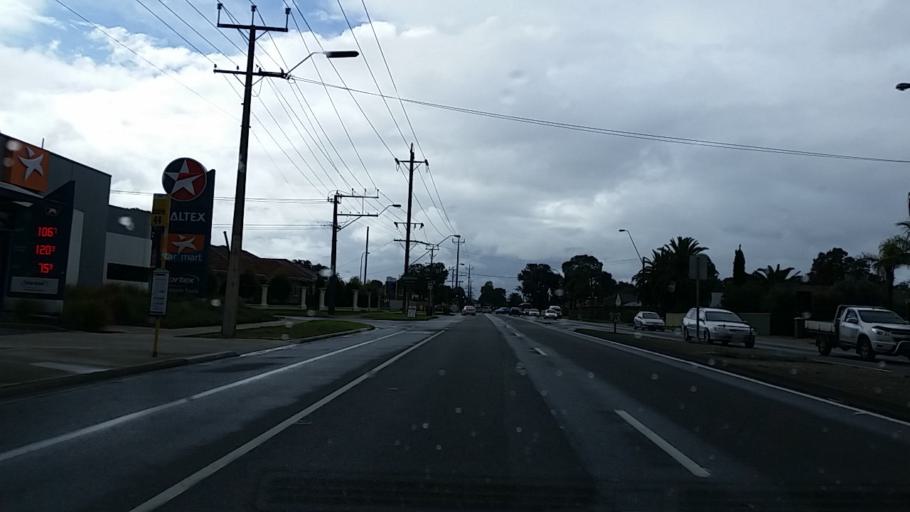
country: AU
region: South Australia
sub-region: Salisbury
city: Salisbury
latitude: -34.7718
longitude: 138.6329
